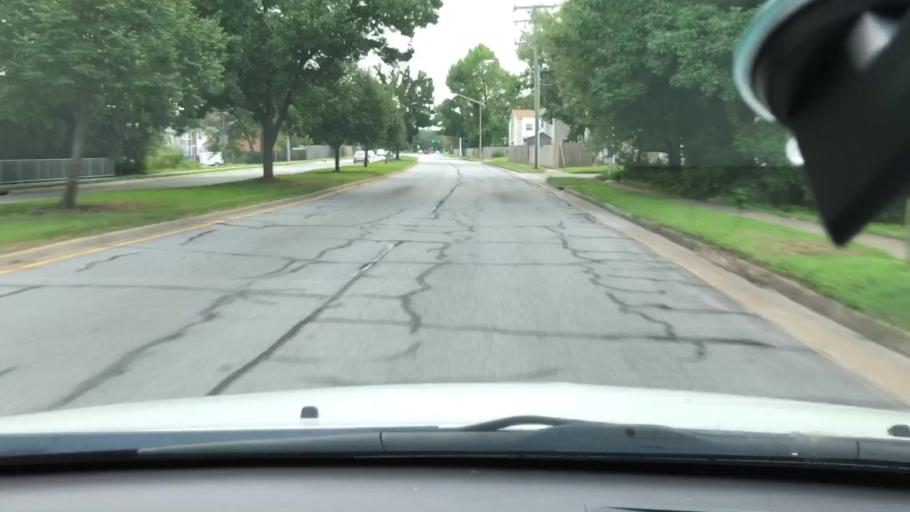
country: US
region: Virginia
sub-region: City of Chesapeake
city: Chesapeake
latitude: 36.8140
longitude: -76.1873
